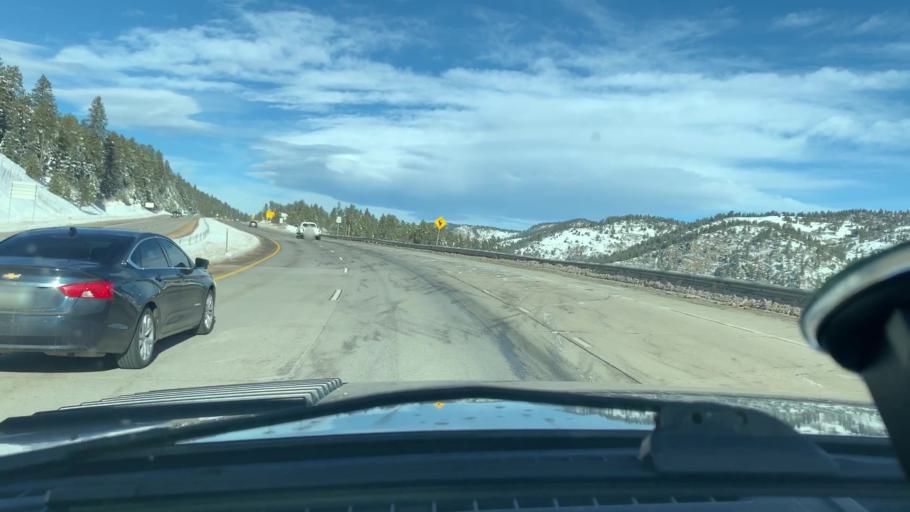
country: US
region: Colorado
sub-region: Jefferson County
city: Indian Hills
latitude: 39.5950
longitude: -105.2228
